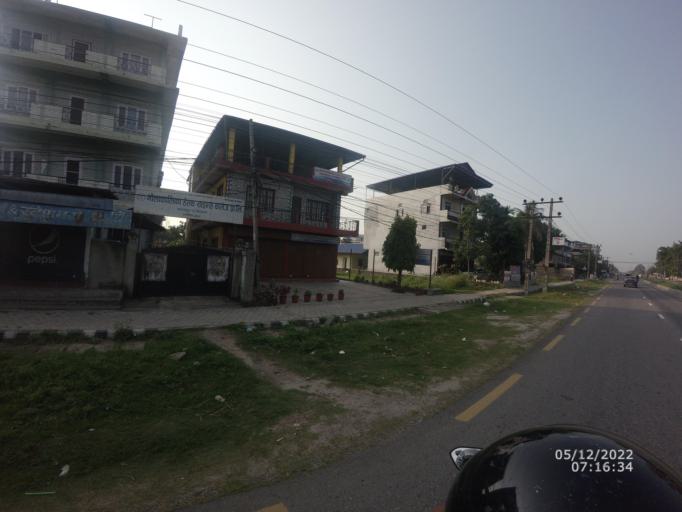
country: NP
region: Central Region
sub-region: Narayani Zone
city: Bharatpur
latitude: 27.6822
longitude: 84.4396
